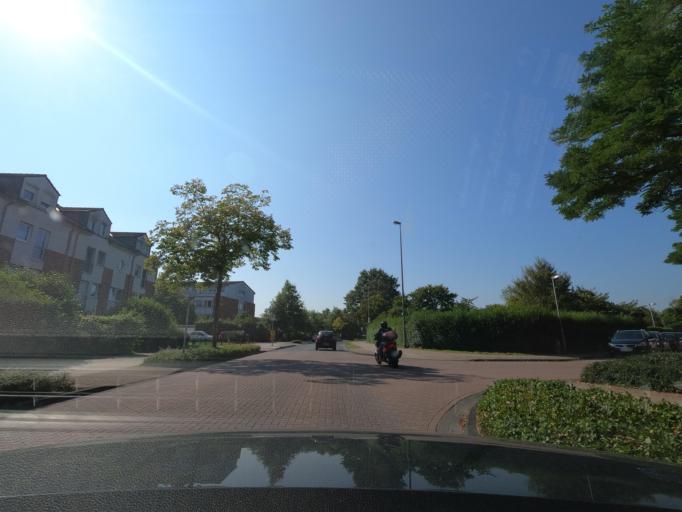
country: DE
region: North Rhine-Westphalia
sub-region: Regierungsbezirk Dusseldorf
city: Dinslaken
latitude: 51.5593
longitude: 6.7813
